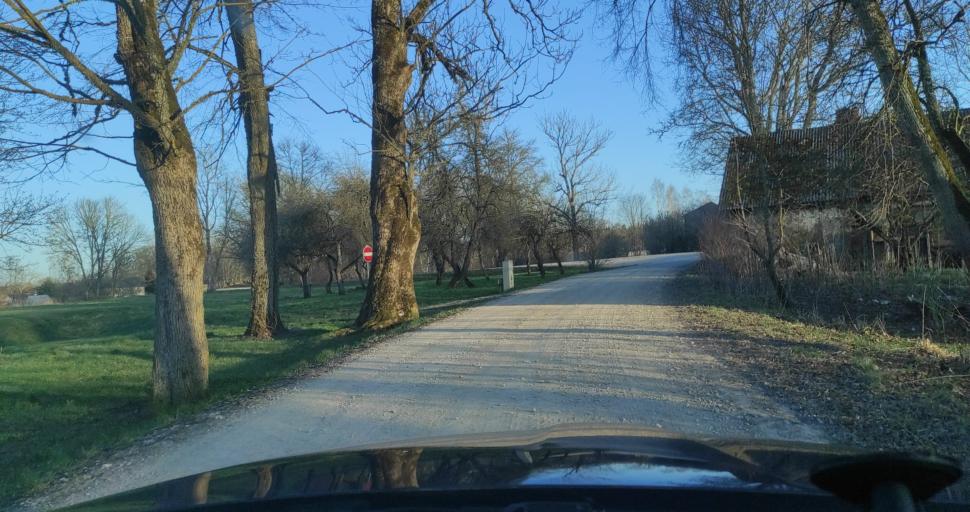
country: LV
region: Aizpute
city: Aizpute
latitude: 56.7346
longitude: 21.7742
